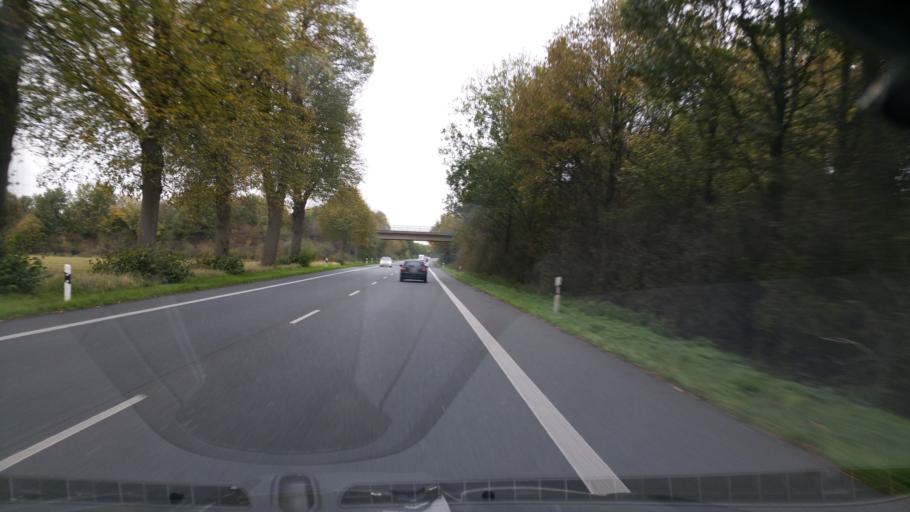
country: DE
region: North Rhine-Westphalia
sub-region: Regierungsbezirk Dusseldorf
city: Hamminkeln
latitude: 51.7589
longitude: 6.5858
